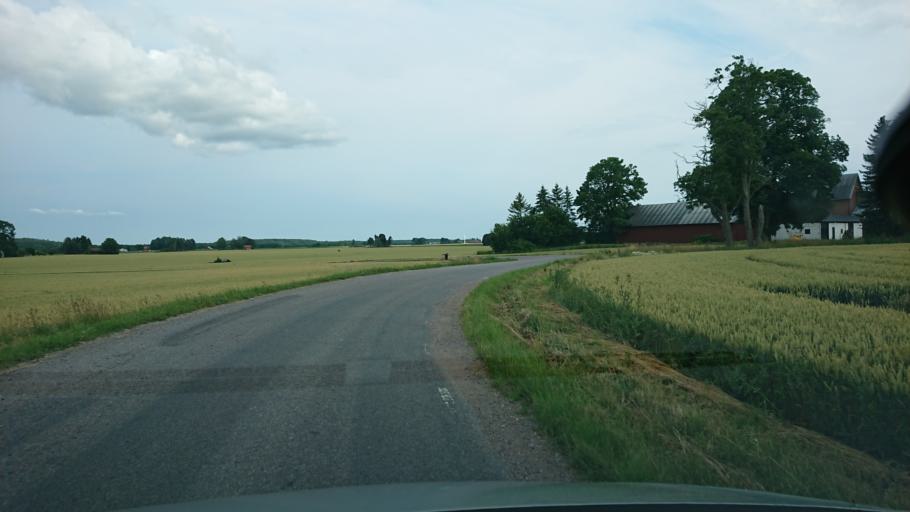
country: SE
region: Uppsala
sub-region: Osthammars Kommun
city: Bjorklinge
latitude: 59.9897
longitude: 17.5312
